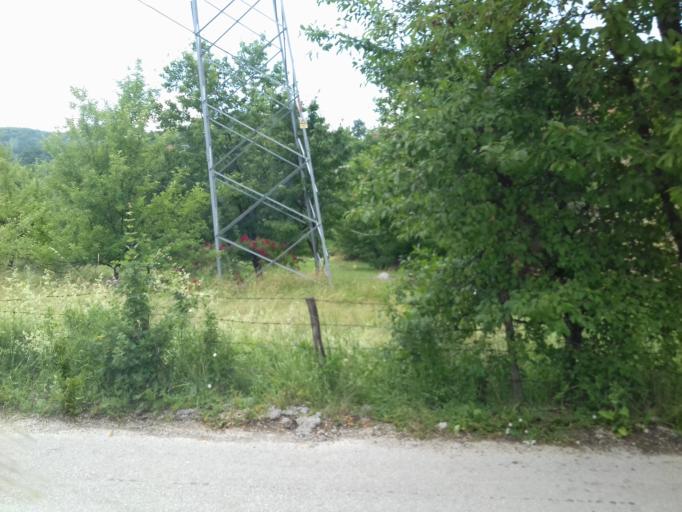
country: BA
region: Federation of Bosnia and Herzegovina
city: Hotonj
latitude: 43.8952
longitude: 18.3617
